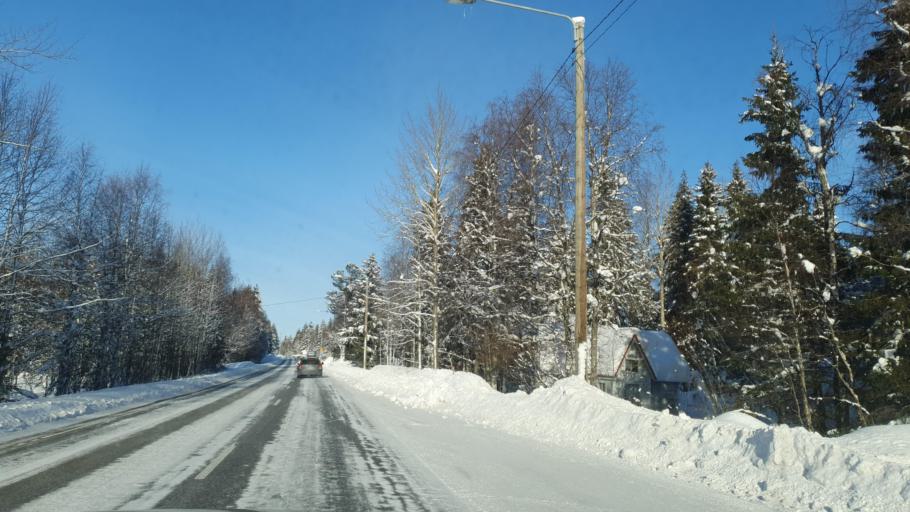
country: FI
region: Lapland
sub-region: Torniolaakso
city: Ylitornio
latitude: 66.1451
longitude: 23.9408
